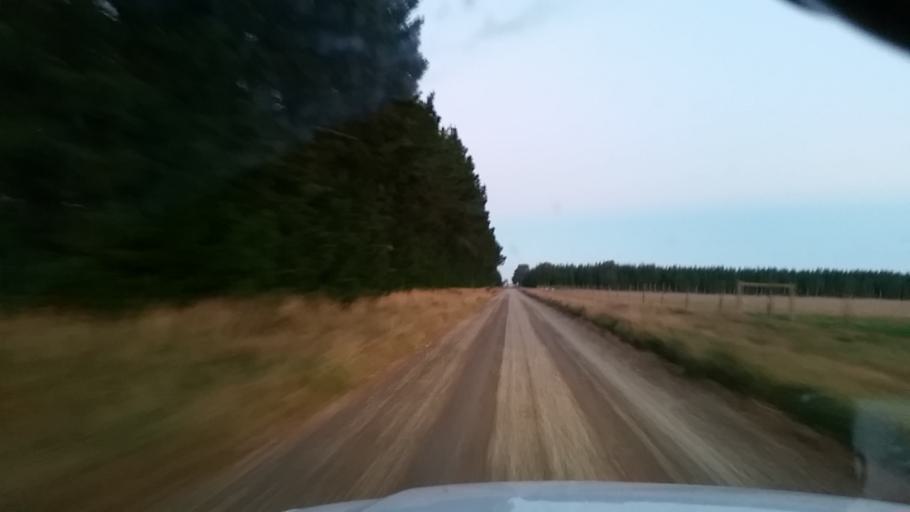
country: NZ
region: Canterbury
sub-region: Ashburton District
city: Tinwald
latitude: -43.9621
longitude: 171.6279
